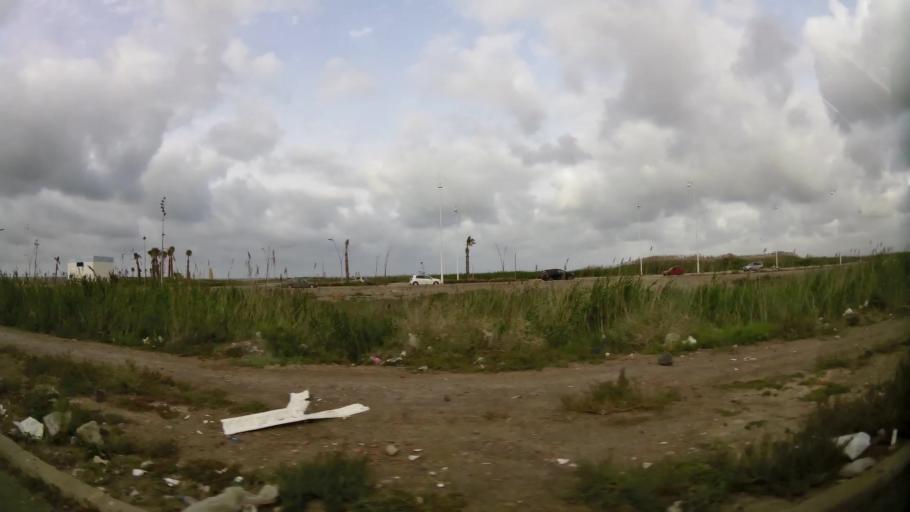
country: MA
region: Oriental
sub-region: Nador
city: Nador
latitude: 35.1567
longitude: -2.9080
